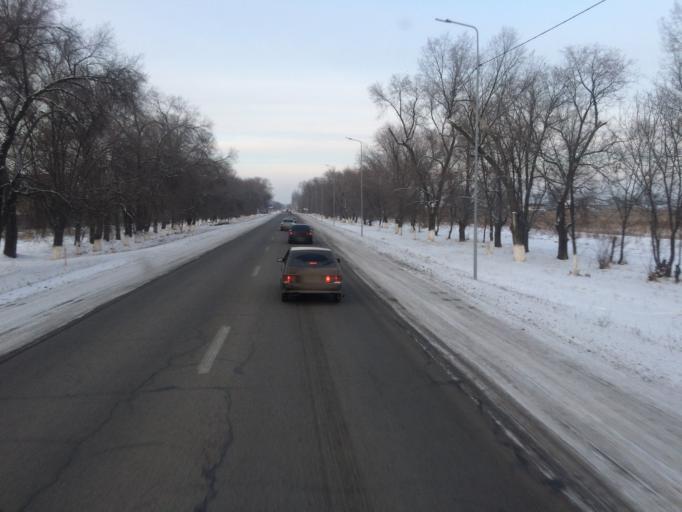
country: KZ
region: Almaty Oblysy
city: Burunday
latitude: 43.2636
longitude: 76.6698
